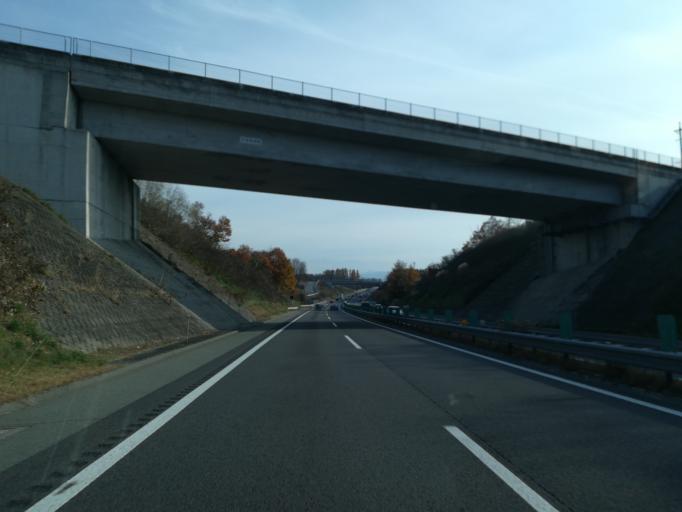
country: JP
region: Nagano
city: Komoro
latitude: 36.3187
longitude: 138.4775
